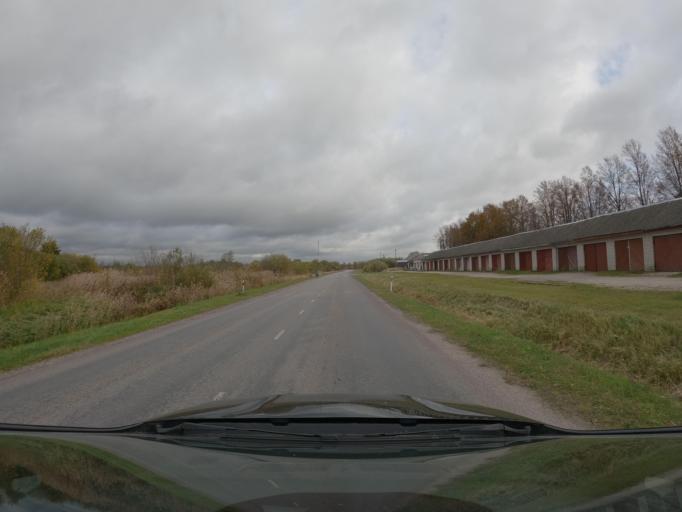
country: EE
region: Saare
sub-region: Kuressaare linn
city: Kuressaare
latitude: 58.2654
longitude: 22.4833
